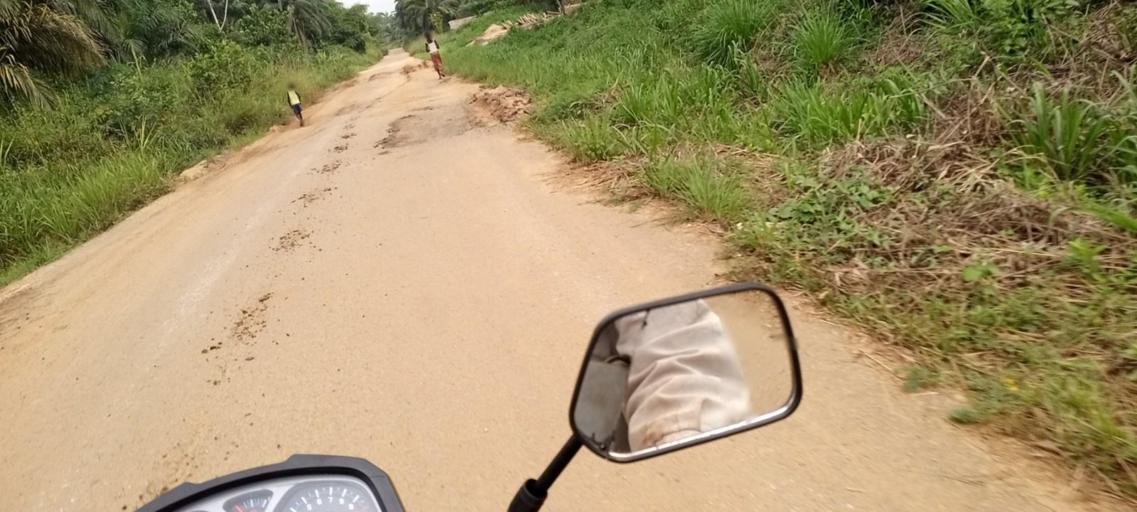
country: CD
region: Eastern Province
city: Kisangani
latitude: 0.2364
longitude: 25.5026
